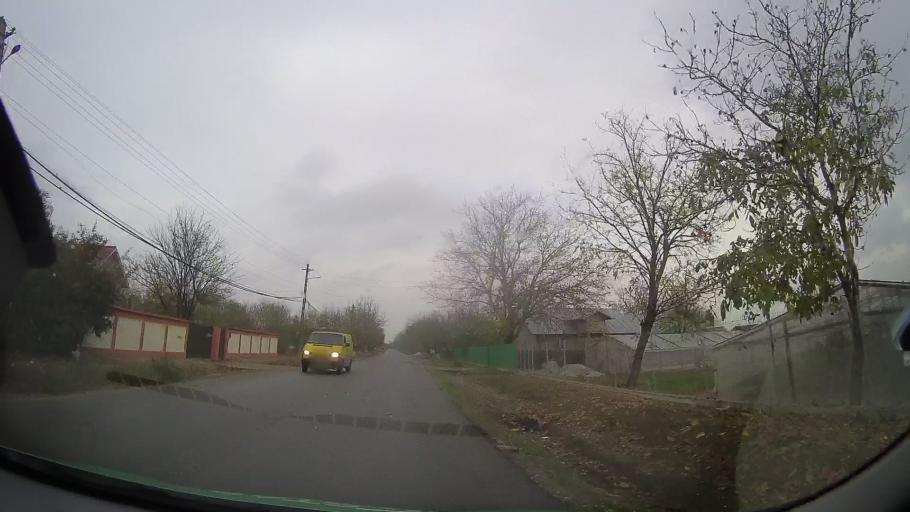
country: RO
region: Prahova
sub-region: Comuna Gherghita
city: Gherghita
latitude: 44.8004
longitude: 26.2789
